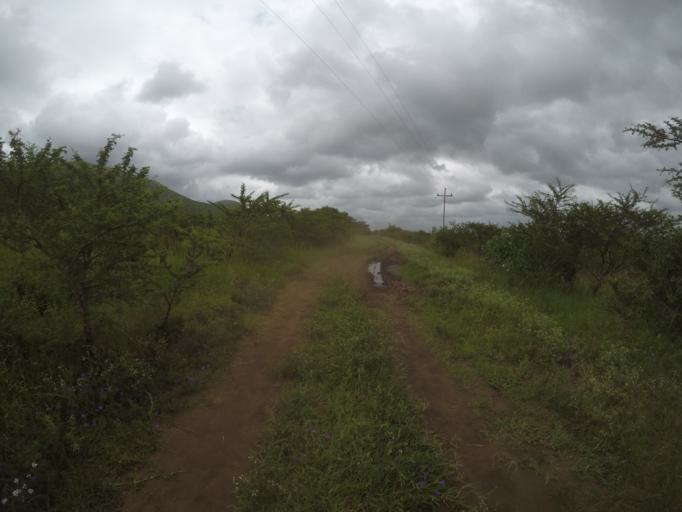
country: ZA
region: KwaZulu-Natal
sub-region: uThungulu District Municipality
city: Empangeni
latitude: -28.5622
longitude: 31.8778
